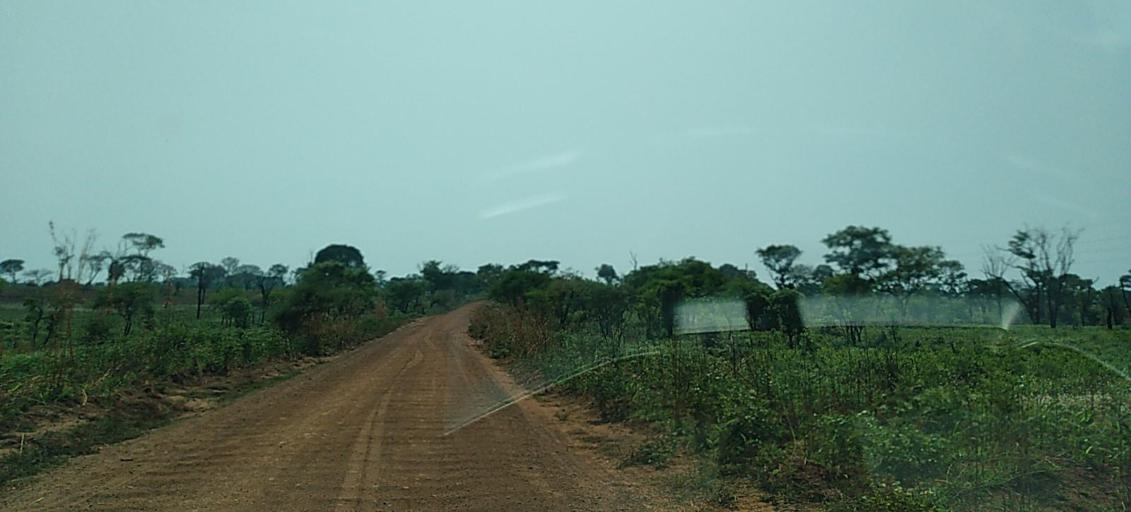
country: ZM
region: North-Western
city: Kansanshi
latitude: -12.0056
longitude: 26.5328
